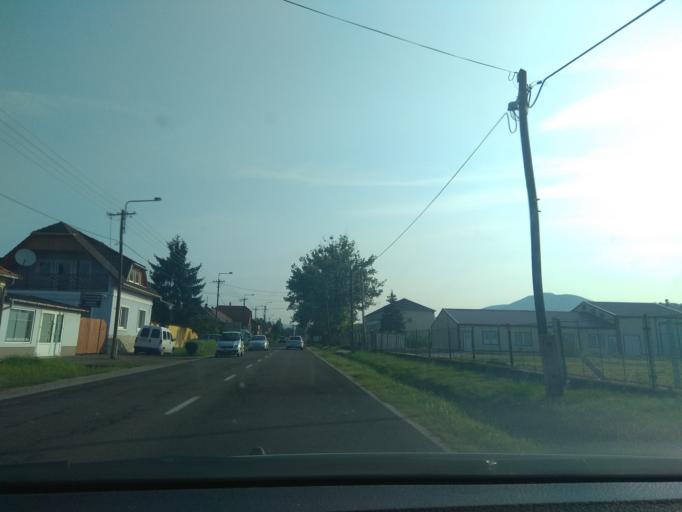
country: HU
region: Heves
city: Eger
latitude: 47.9383
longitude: 20.3710
